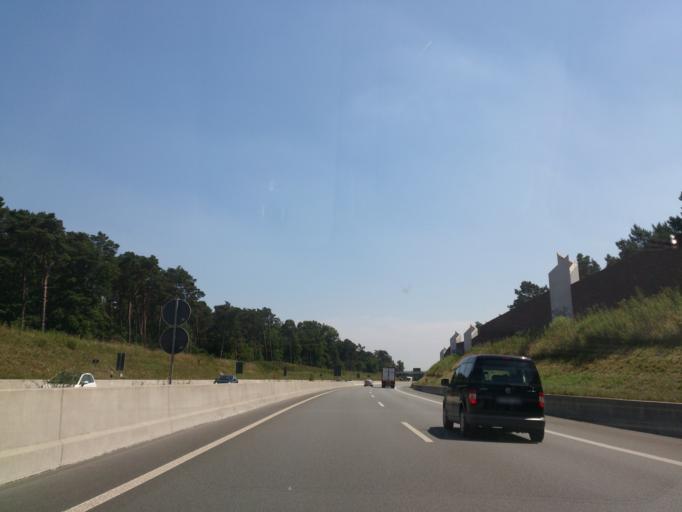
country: DE
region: North Rhine-Westphalia
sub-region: Regierungsbezirk Detmold
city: Bielefeld
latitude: 51.9699
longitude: 8.4902
